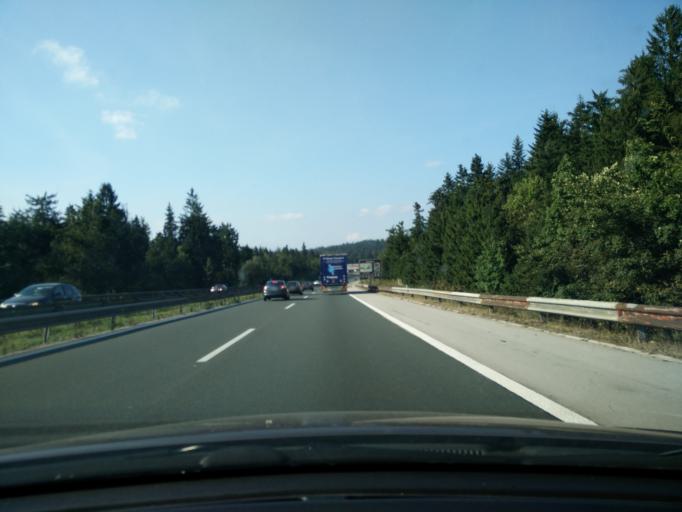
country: SI
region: Logatec
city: Logatec
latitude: 45.8918
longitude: 14.2574
